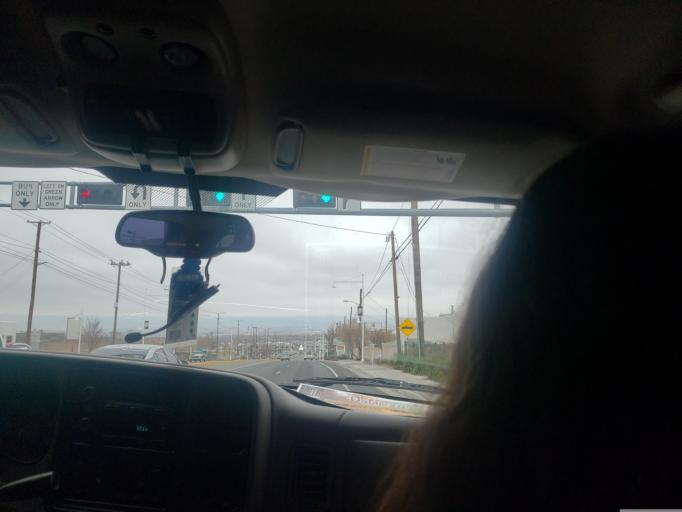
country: US
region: New Mexico
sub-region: Bernalillo County
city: Albuquerque
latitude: 35.0816
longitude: -106.7023
